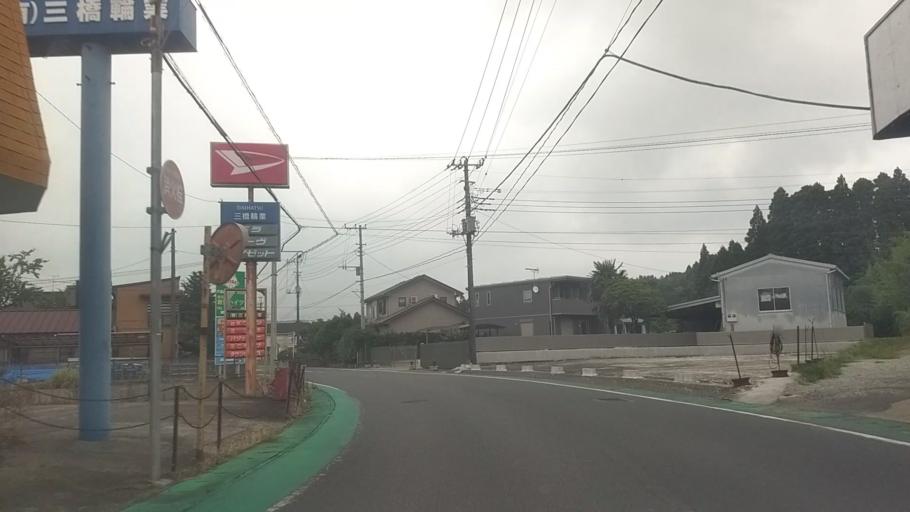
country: JP
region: Chiba
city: Ohara
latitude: 35.2817
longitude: 140.3163
